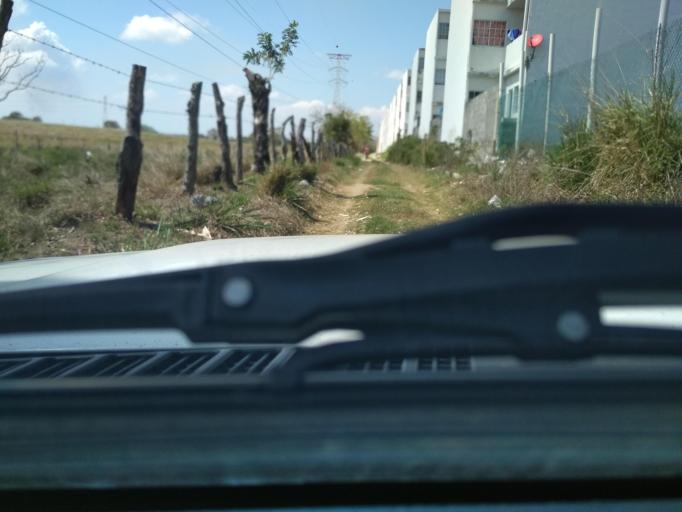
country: MX
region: Veracruz
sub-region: Veracruz
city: Las Amapolas
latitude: 19.1369
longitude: -96.2204
